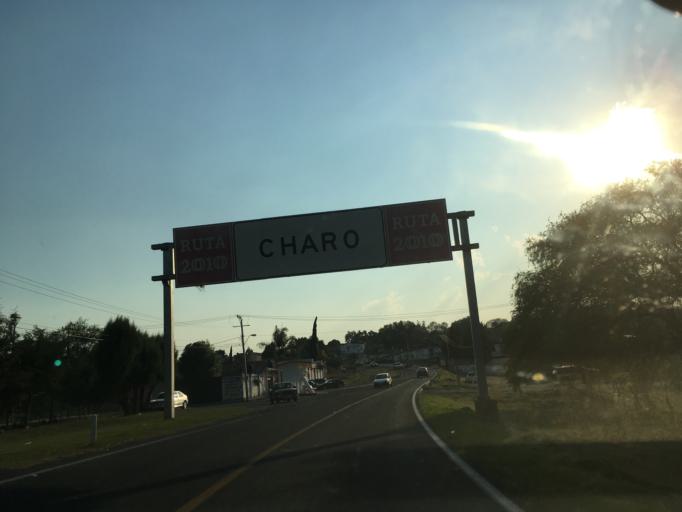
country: MX
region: Michoacan
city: Charo
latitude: 19.7530
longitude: -101.0446
